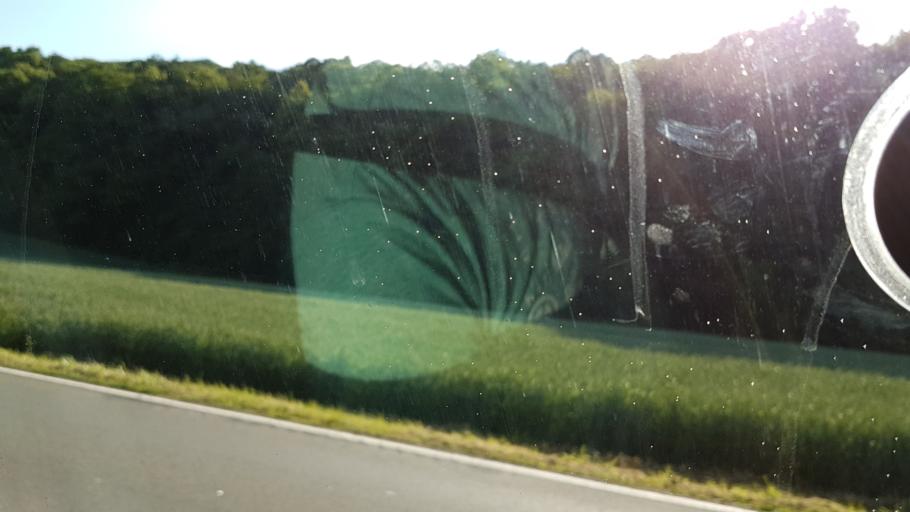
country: DE
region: Rheinland-Pfalz
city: Kalkofen
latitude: 49.7496
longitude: 7.8192
